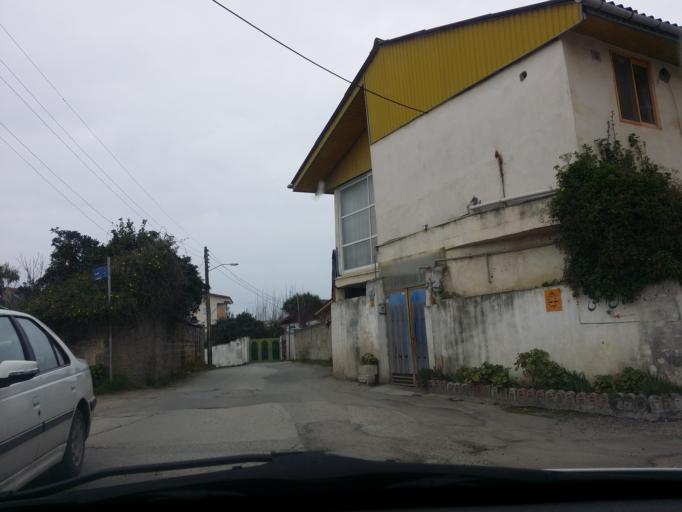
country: IR
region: Mazandaran
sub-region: Nowshahr
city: Nowshahr
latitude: 36.6555
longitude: 51.4776
